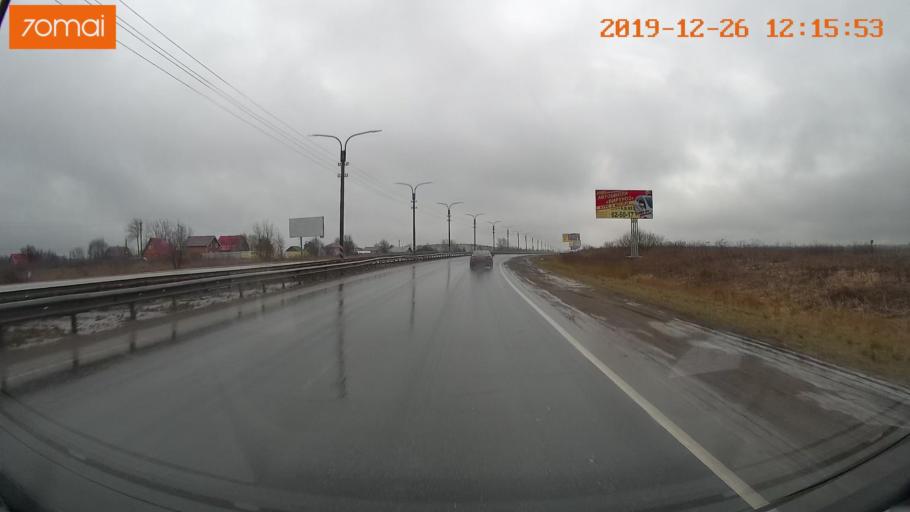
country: RU
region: Vologda
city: Tonshalovo
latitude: 59.2027
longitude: 37.9419
